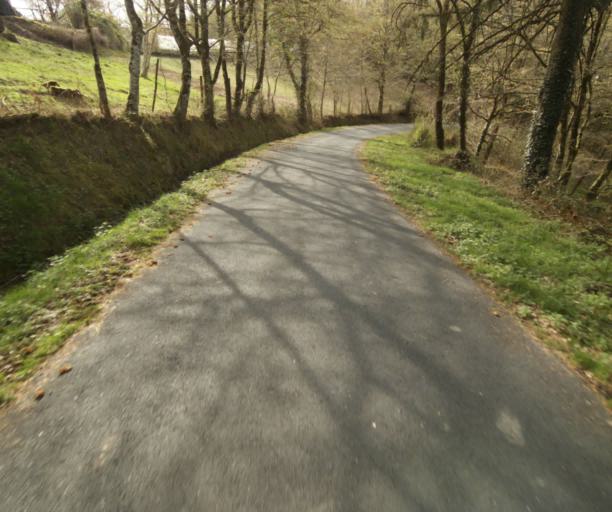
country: FR
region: Limousin
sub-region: Departement de la Correze
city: Chamboulive
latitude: 45.4315
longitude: 1.7912
